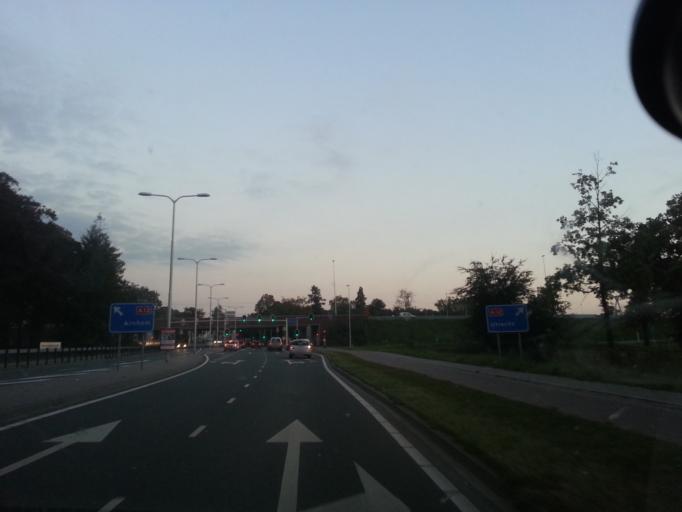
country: NL
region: Utrecht
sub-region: Gemeente Utrechtse Heuvelrug
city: Driebergen-Rijsenburg
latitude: 52.0623
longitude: 5.2649
